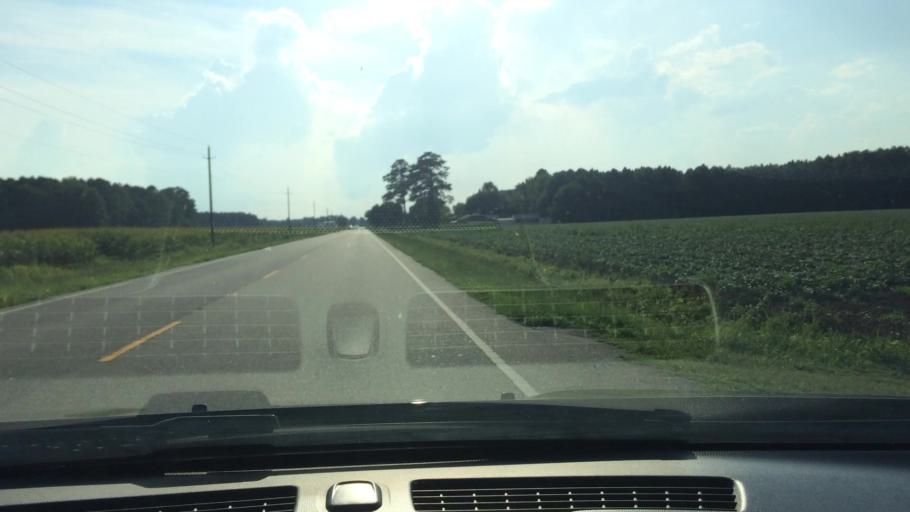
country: US
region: North Carolina
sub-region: Pitt County
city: Ayden
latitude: 35.4708
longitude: -77.3774
